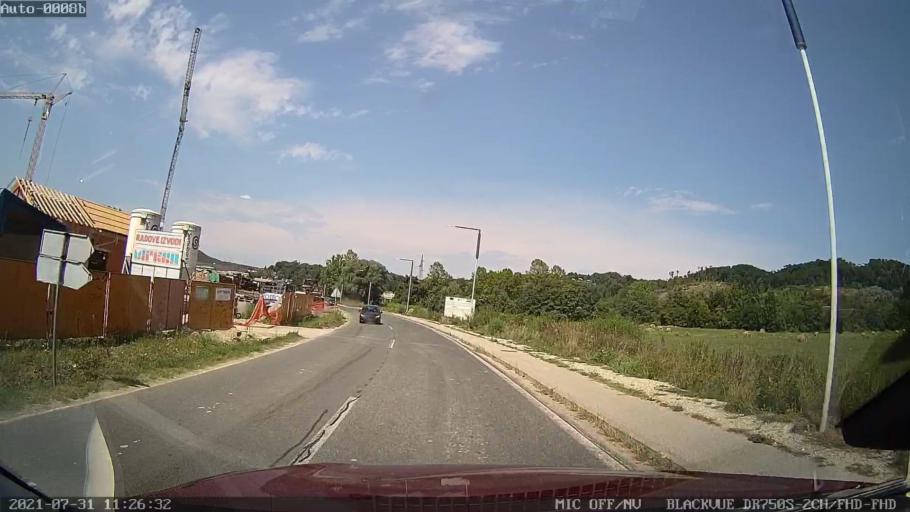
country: HR
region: Varazdinska
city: Jalzabet
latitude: 46.2107
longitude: 16.4401
